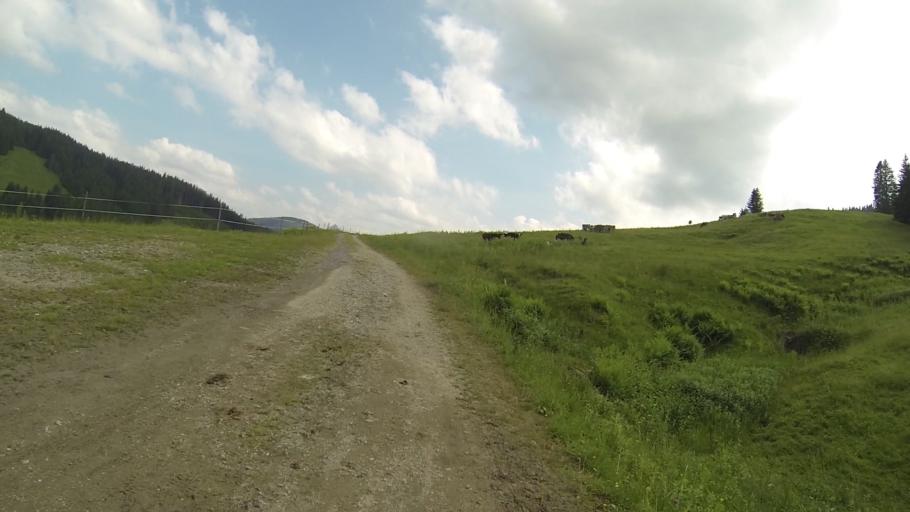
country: AT
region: Tyrol
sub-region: Politischer Bezirk Reutte
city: Jungholz
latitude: 47.5840
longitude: 10.4681
